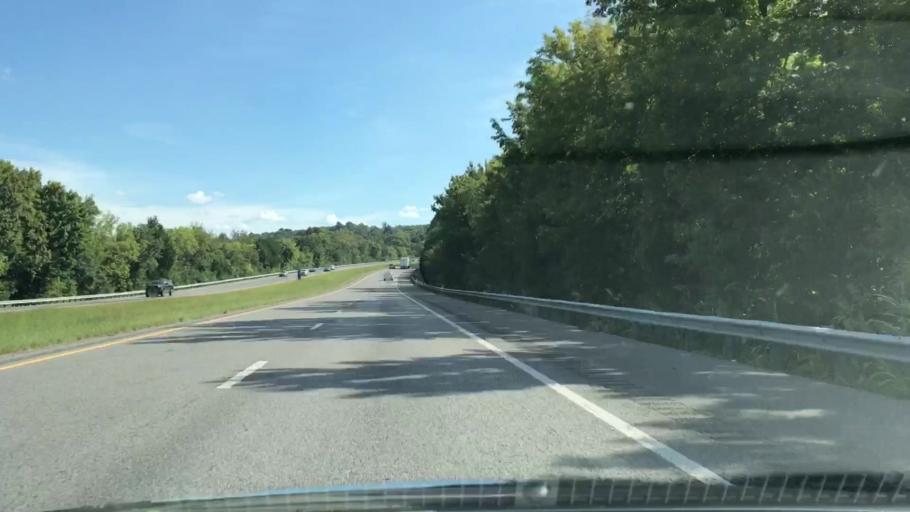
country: US
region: Alabama
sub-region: Limestone County
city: Ardmore
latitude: 35.1286
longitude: -86.8775
